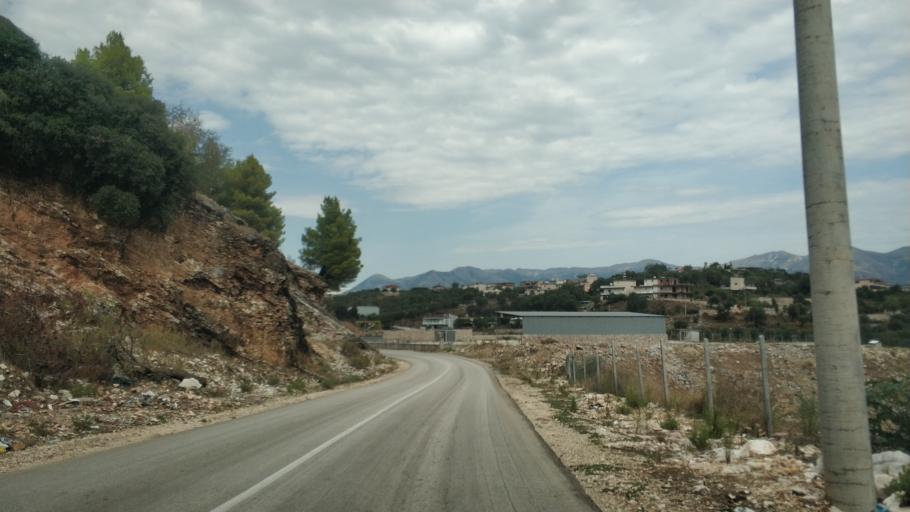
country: AL
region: Vlore
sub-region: Rrethi i Sarandes
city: Sarande
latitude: 39.8682
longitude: 20.0309
